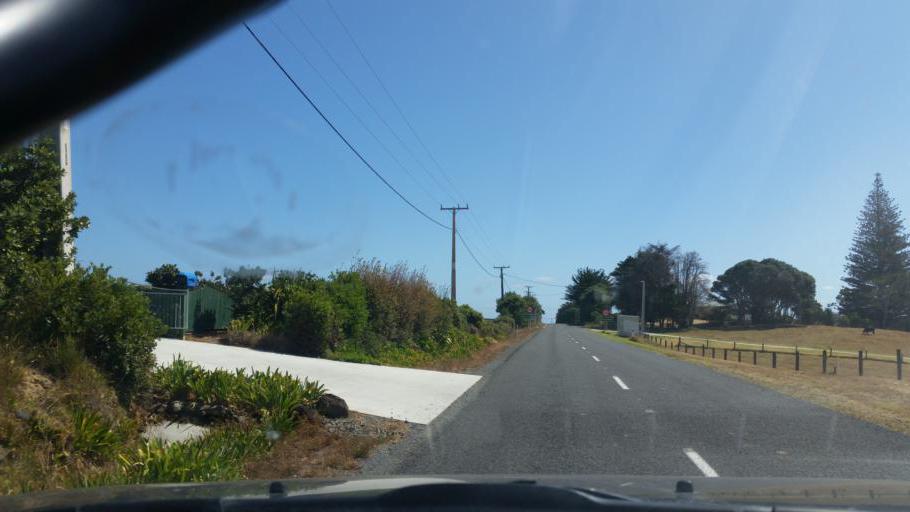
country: NZ
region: Northland
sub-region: Kaipara District
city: Dargaville
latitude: -35.9503
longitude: 173.7543
